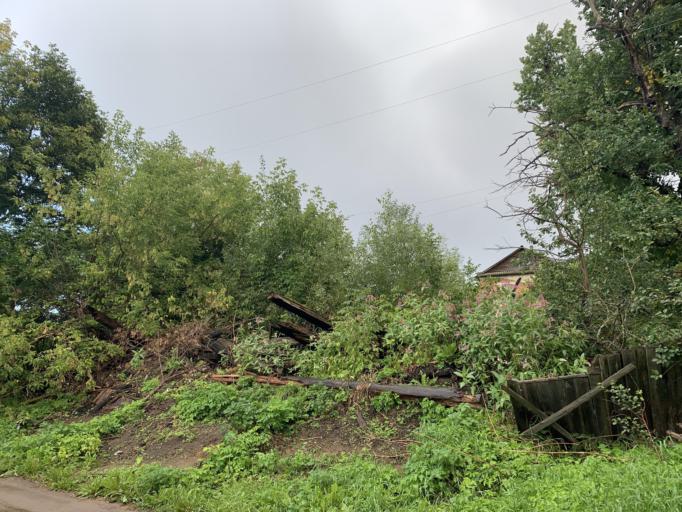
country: RU
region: Tverskaya
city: Vyshniy Volochek
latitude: 57.5824
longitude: 34.5499
